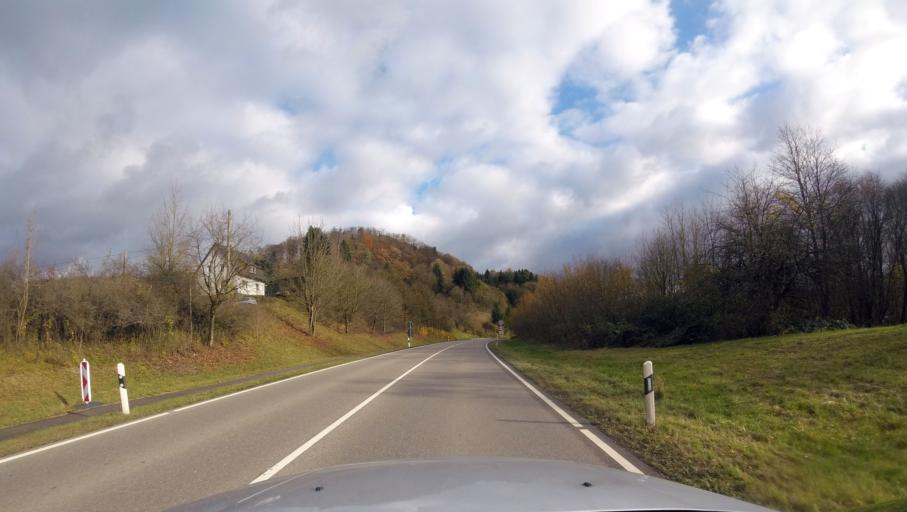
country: DE
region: Baden-Wuerttemberg
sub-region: Regierungsbezirk Stuttgart
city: Murrhardt
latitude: 48.9889
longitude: 9.5546
